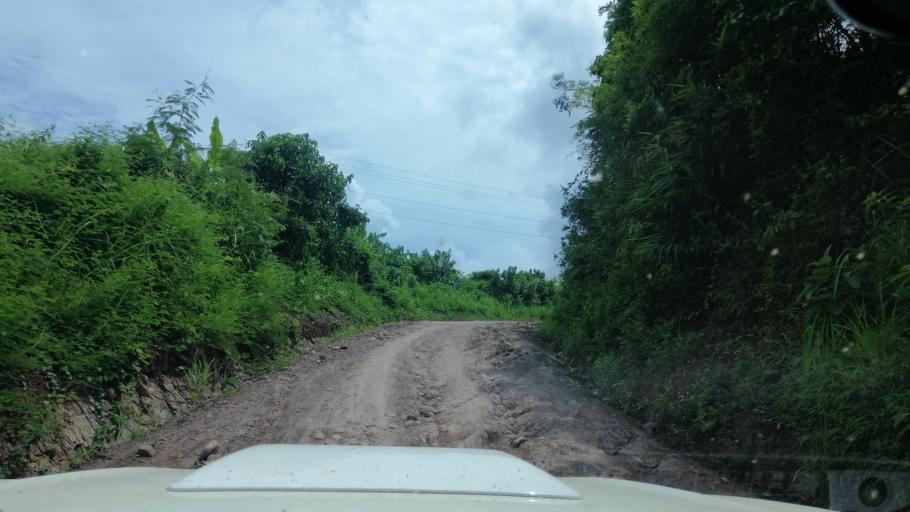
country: LA
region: Xiagnabouli
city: Sainyabuli
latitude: 18.9011
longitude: 101.4925
